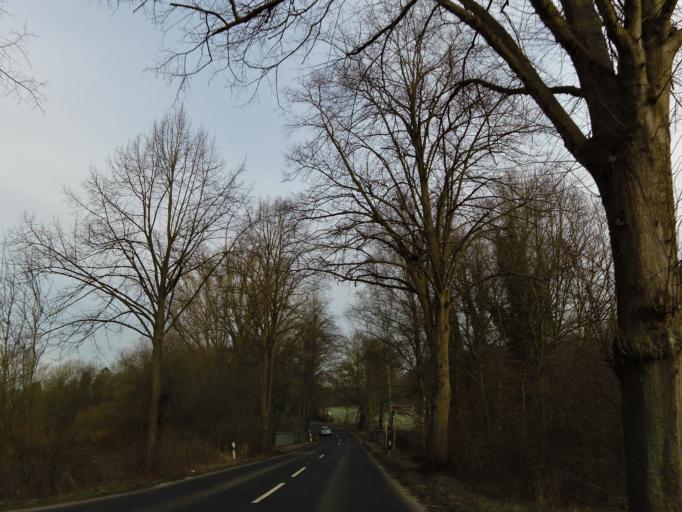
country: DE
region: North Rhine-Westphalia
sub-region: Regierungsbezirk Koln
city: Herzogenrath
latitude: 50.8411
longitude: 6.0988
